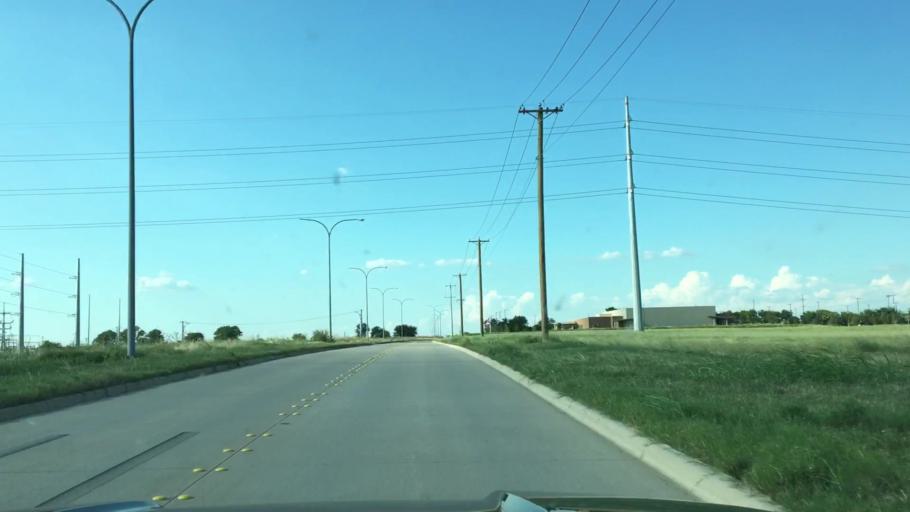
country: US
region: Texas
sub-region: Tarrant County
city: Haslet
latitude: 32.9968
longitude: -97.3589
